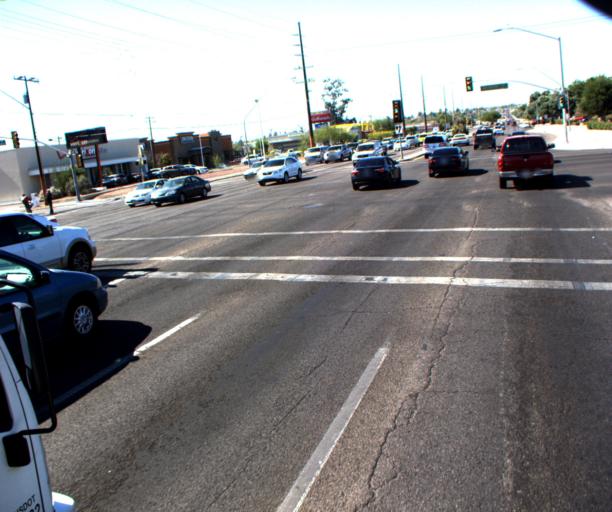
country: US
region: Arizona
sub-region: Pima County
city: Flowing Wells
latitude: 32.2862
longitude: -110.9781
